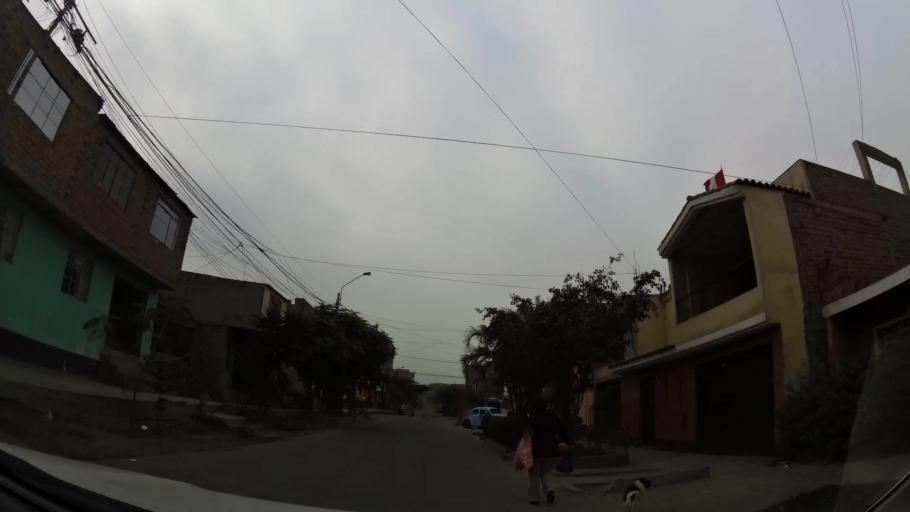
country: PE
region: Lima
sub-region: Lima
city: Independencia
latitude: -11.9838
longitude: -77.0160
